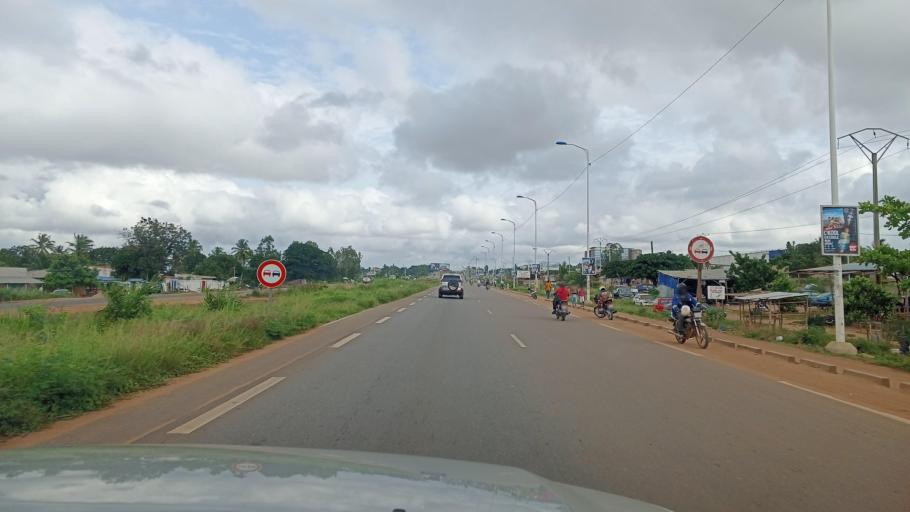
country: TG
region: Maritime
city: Tsevie
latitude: 6.3302
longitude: 1.2181
